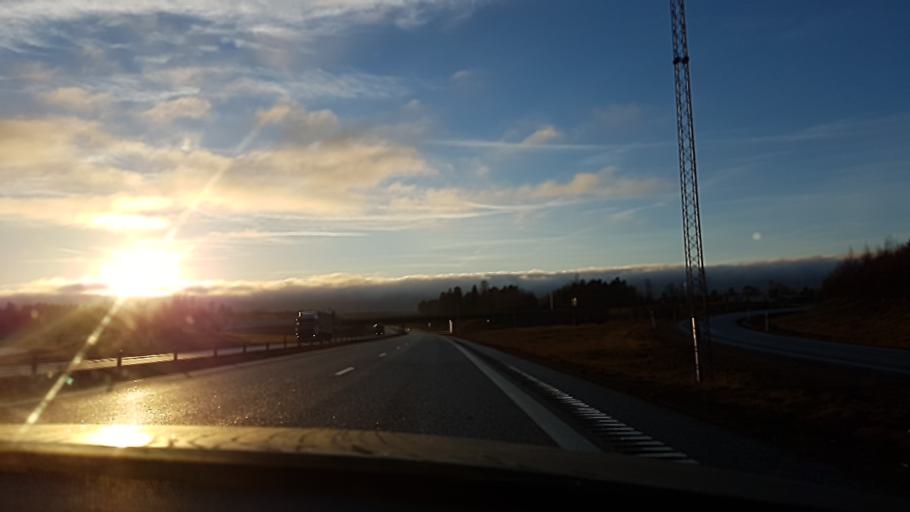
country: SE
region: Kronoberg
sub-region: Markaryds Kommun
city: Markaryd
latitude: 56.4489
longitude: 13.6043
